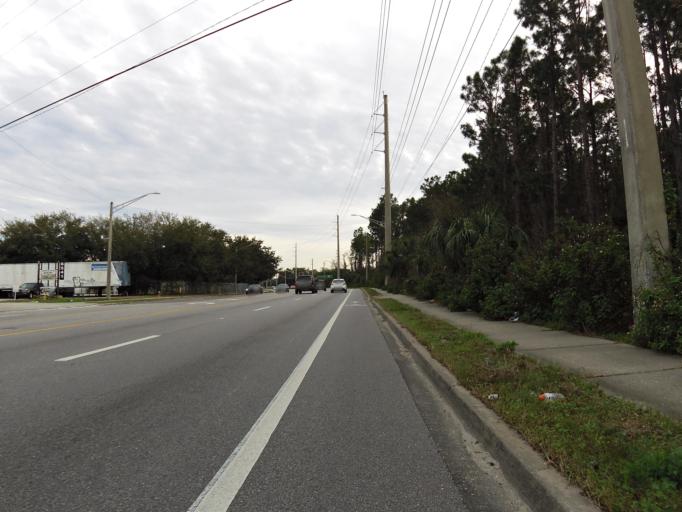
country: US
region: Florida
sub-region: Duval County
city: Jacksonville
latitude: 30.2553
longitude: -81.6171
